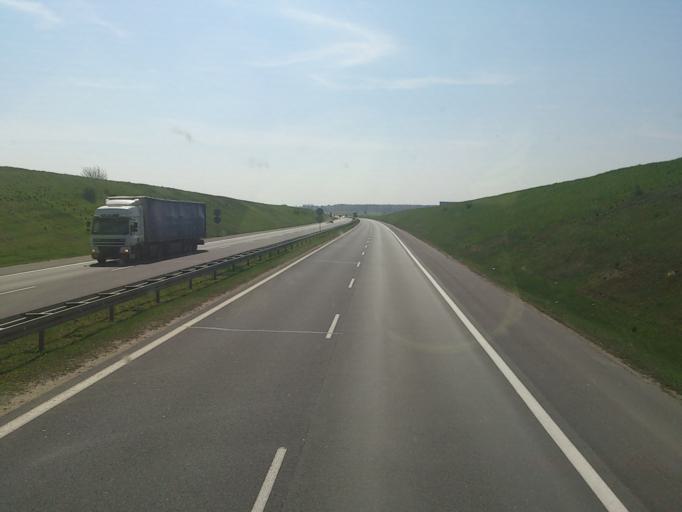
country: PL
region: Lodz Voivodeship
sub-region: Powiat piotrkowski
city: Grabica
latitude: 51.5334
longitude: 19.6001
